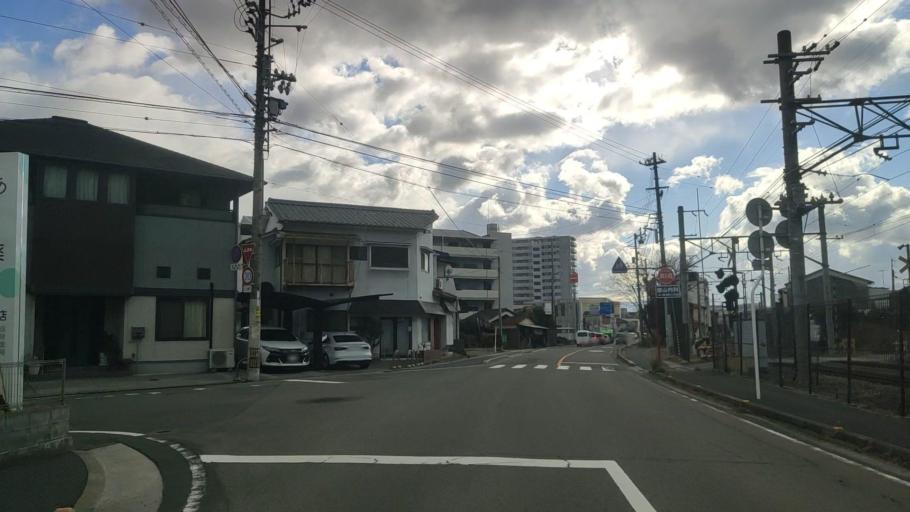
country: JP
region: Ehime
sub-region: Shikoku-chuo Shi
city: Matsuyama
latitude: 33.8689
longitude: 132.7172
